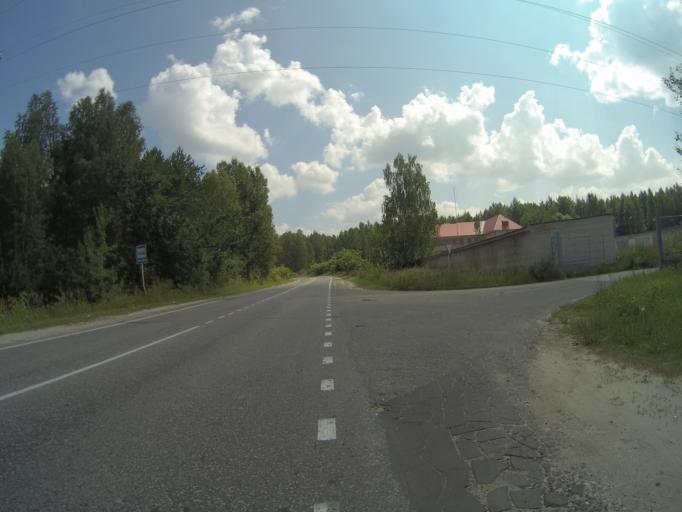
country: RU
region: Vladimir
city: Gus'-Khrustal'nyy
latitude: 55.6361
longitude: 40.7145
